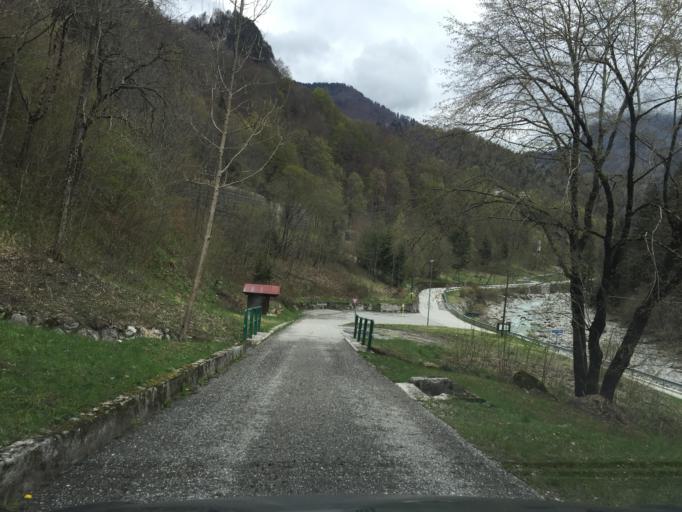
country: IT
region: Friuli Venezia Giulia
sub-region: Provincia di Udine
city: Moggio Udinese
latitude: 46.4877
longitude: 13.1940
